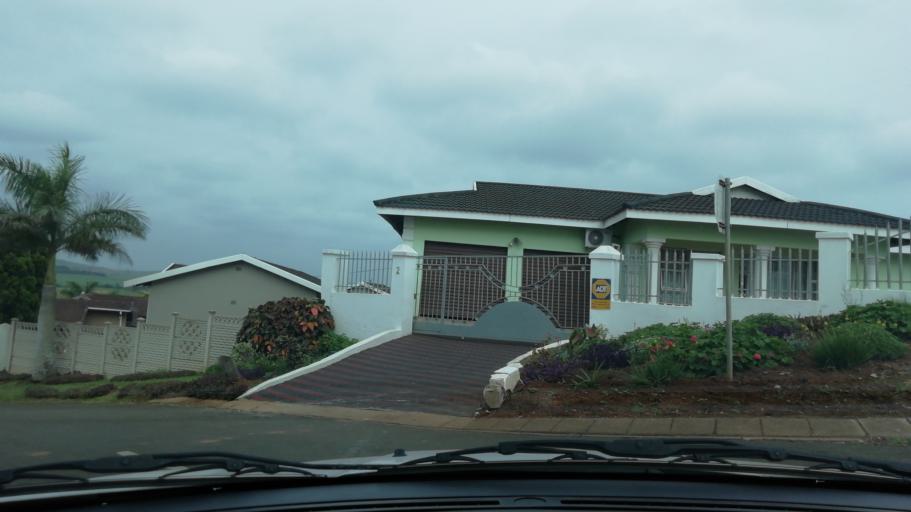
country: ZA
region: KwaZulu-Natal
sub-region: uThungulu District Municipality
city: Empangeni
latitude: -28.7381
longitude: 31.8778
